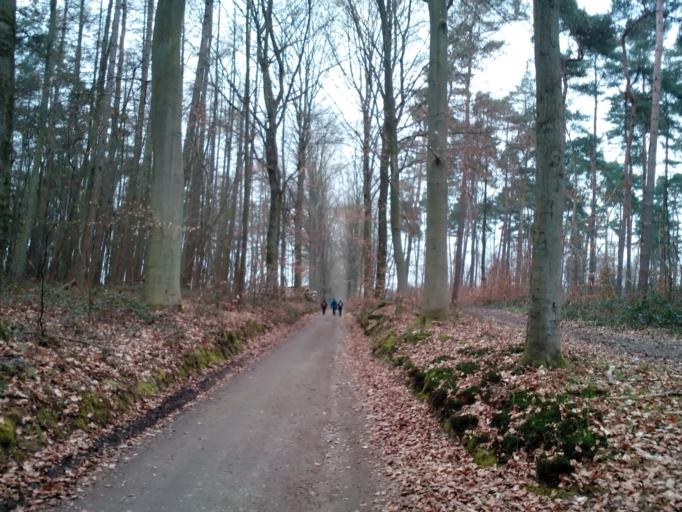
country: BE
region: Flanders
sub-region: Provincie Vlaams-Brabant
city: Oud-Heverlee
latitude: 50.8128
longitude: 4.6650
